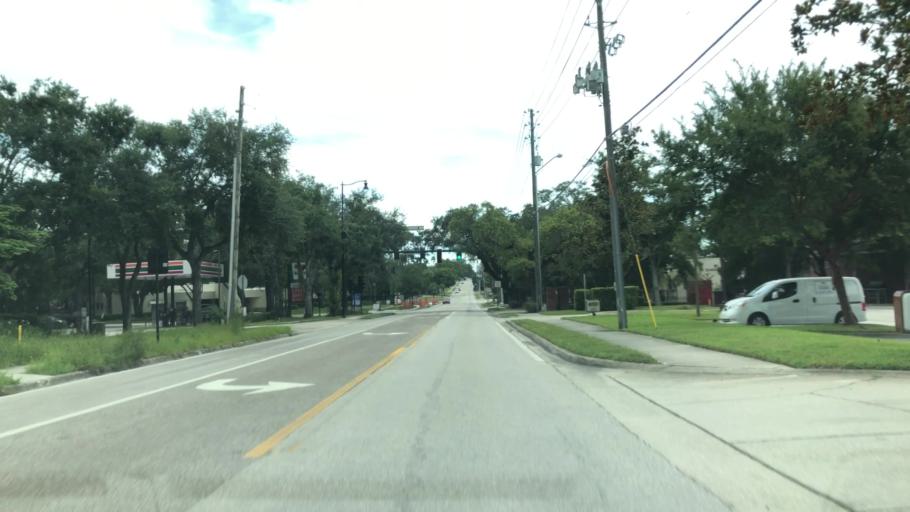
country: US
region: Florida
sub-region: Seminole County
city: Altamonte Springs
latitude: 28.6655
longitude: -81.3903
